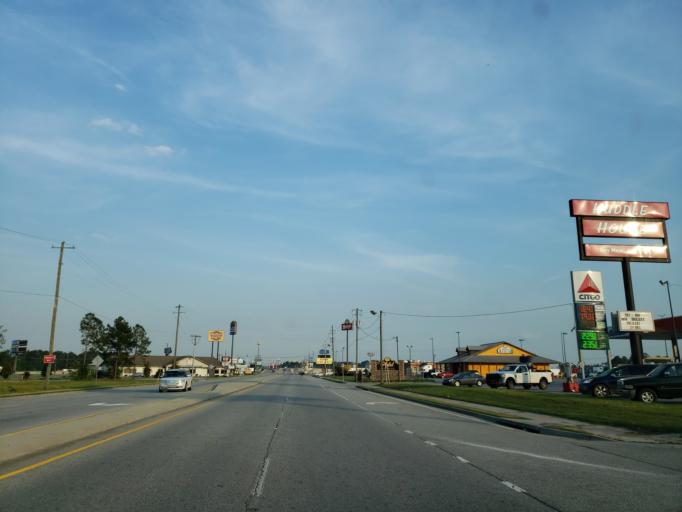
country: US
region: Georgia
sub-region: Cook County
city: Adel
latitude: 31.1391
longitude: -83.4449
